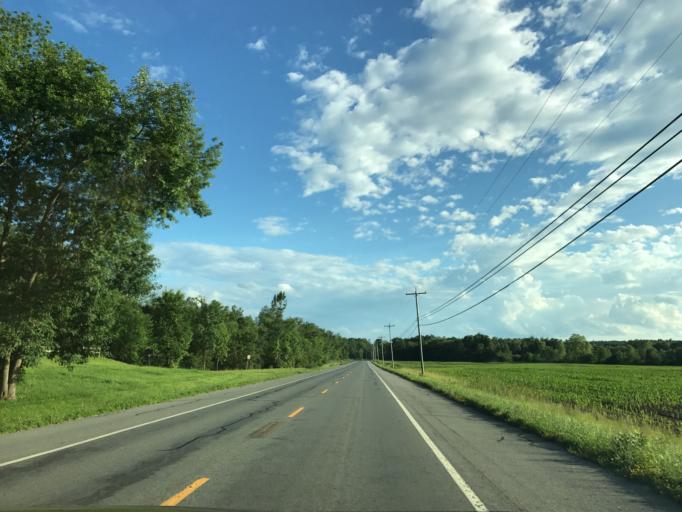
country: US
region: New York
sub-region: Saratoga County
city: Schuylerville
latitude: 43.1493
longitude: -73.5779
